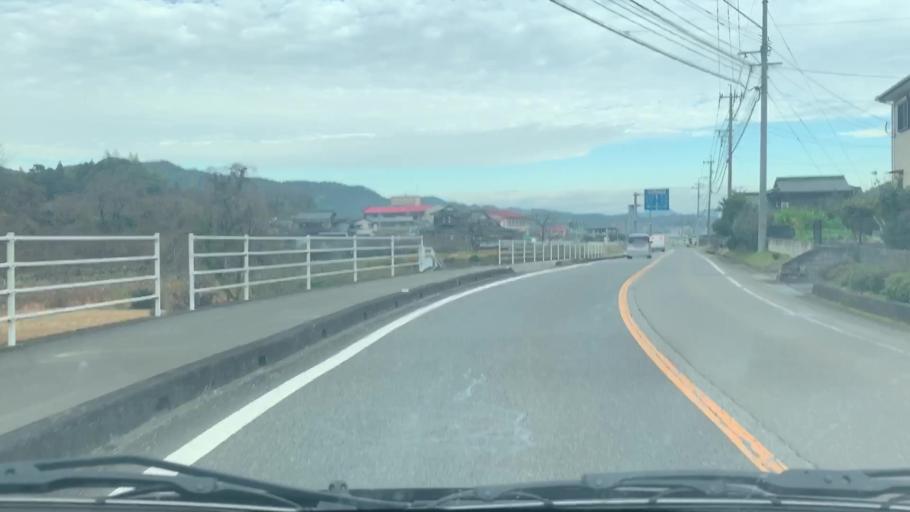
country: JP
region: Saga Prefecture
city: Takeocho-takeo
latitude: 33.1905
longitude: 129.9656
